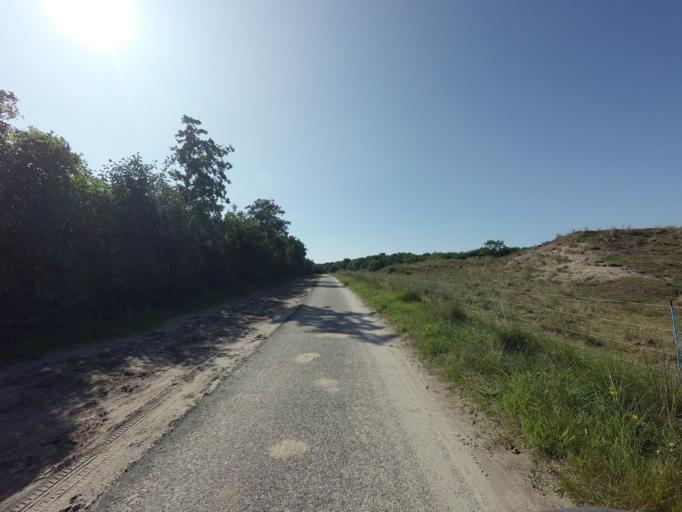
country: NL
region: Friesland
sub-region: Gemeente Terschelling
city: West-Terschelling
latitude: 53.3950
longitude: 5.3173
